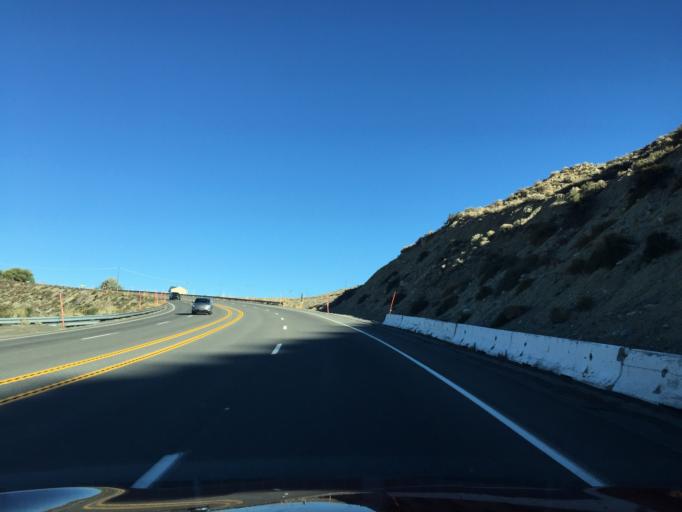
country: US
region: California
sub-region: Mono County
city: Bridgeport
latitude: 38.0831
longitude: -119.1781
